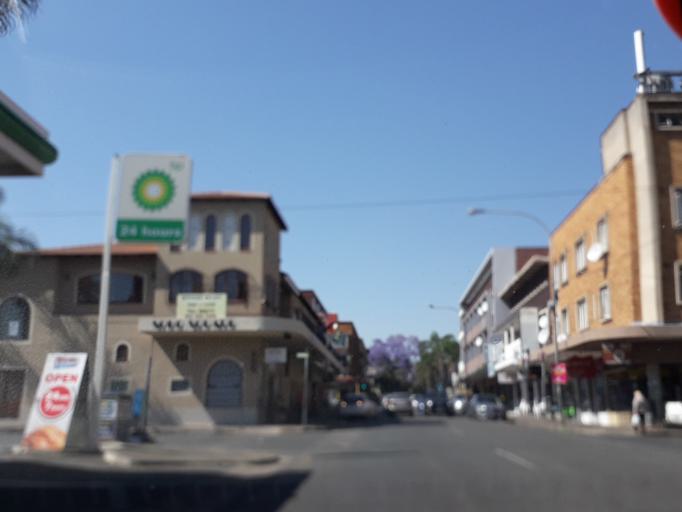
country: ZA
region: Gauteng
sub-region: City of Johannesburg Metropolitan Municipality
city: Johannesburg
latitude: -26.1593
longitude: 28.0763
